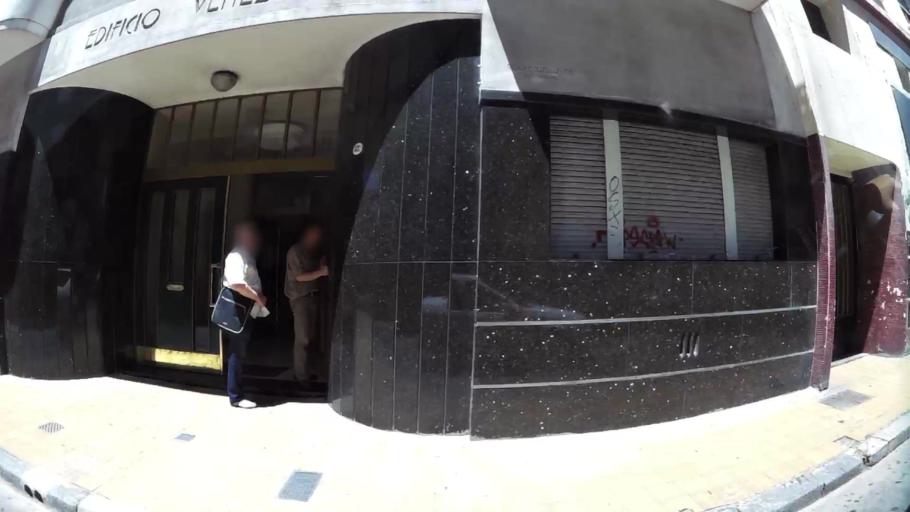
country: AR
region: Buenos Aires F.D.
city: Buenos Aires
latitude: -34.6136
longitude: -58.3726
